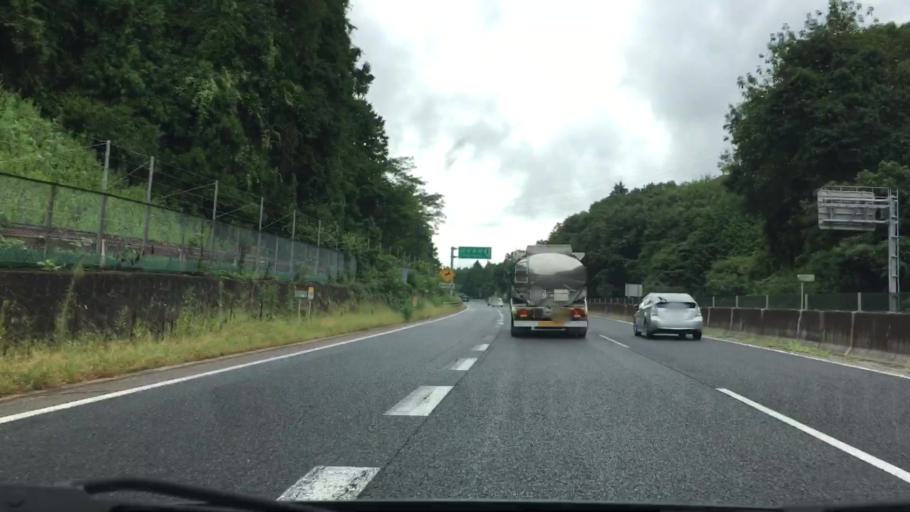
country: JP
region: Hyogo
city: Yamazakicho-nakabirose
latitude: 35.0337
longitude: 134.4828
